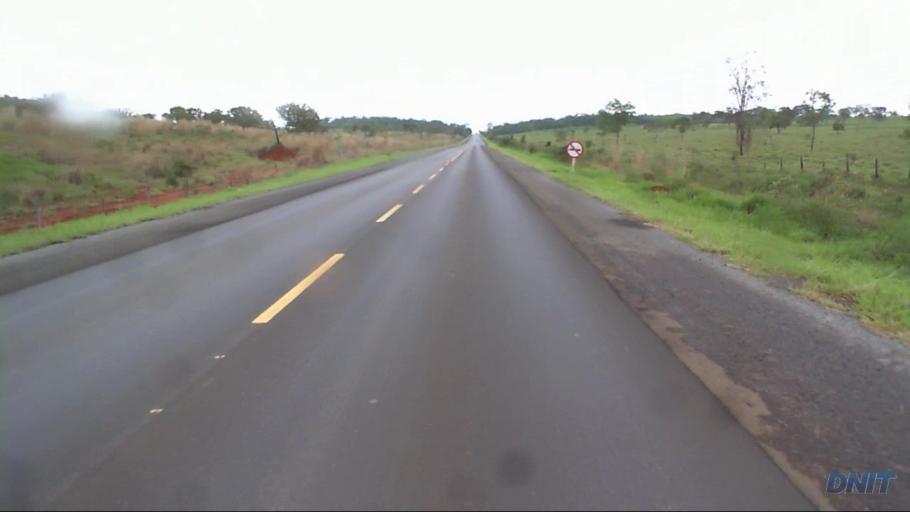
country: BR
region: Goias
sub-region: Padre Bernardo
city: Padre Bernardo
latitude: -15.2090
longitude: -48.4708
